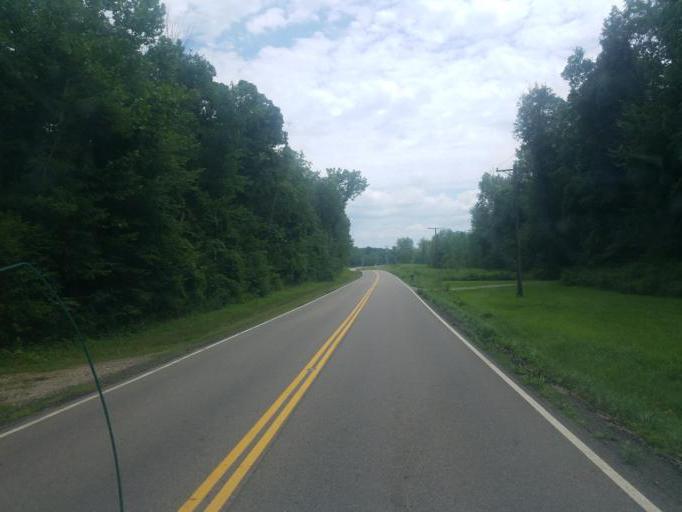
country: US
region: Ohio
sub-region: Licking County
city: Utica
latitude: 40.2075
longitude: -82.5386
